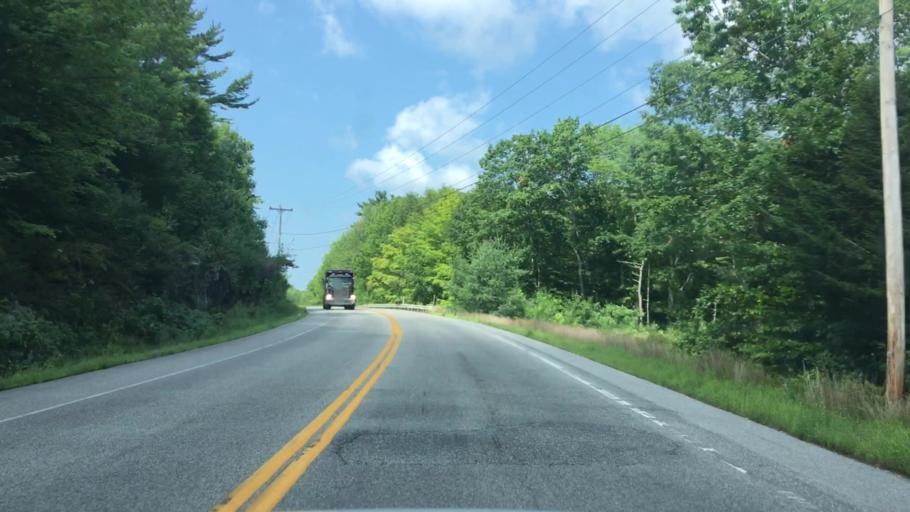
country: US
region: Maine
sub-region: Androscoggin County
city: Minot
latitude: 44.0285
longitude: -70.3112
